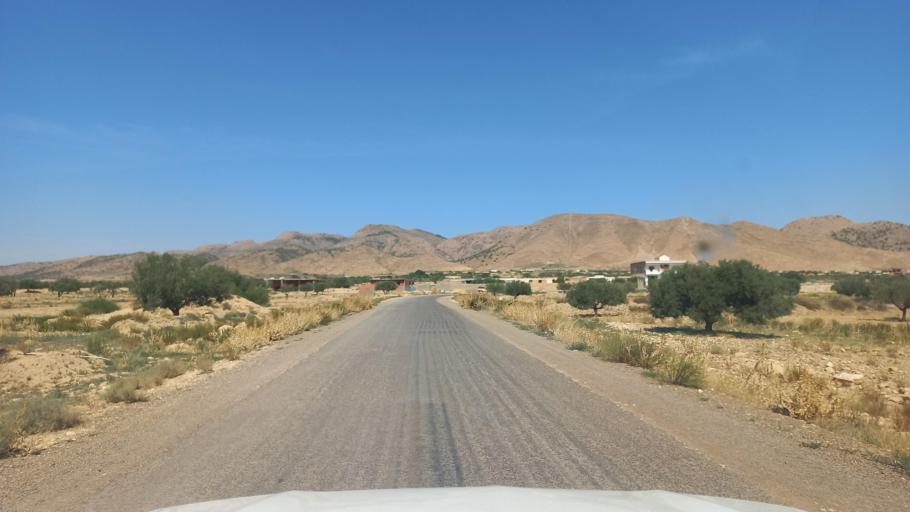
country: TN
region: Al Qasrayn
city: Sbiba
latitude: 35.4409
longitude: 9.0747
